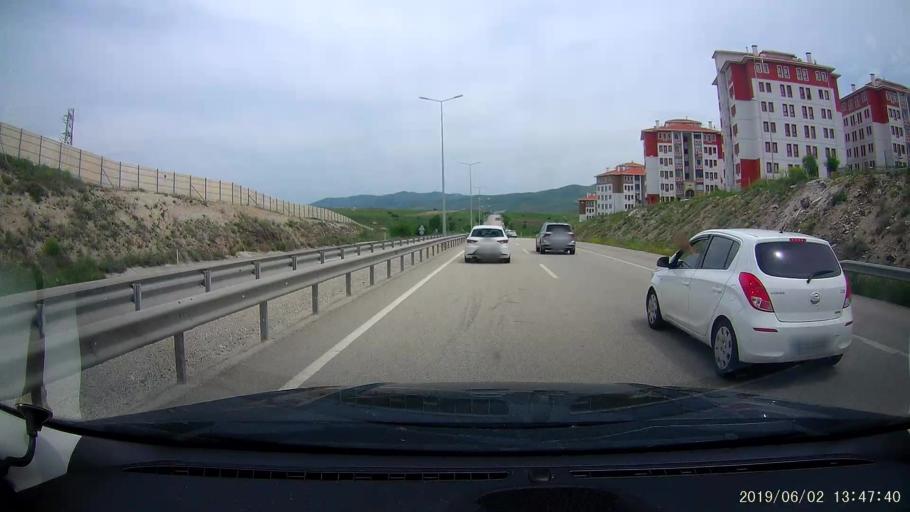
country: TR
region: Cankiri
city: Kursunlu
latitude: 40.8391
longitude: 33.2878
